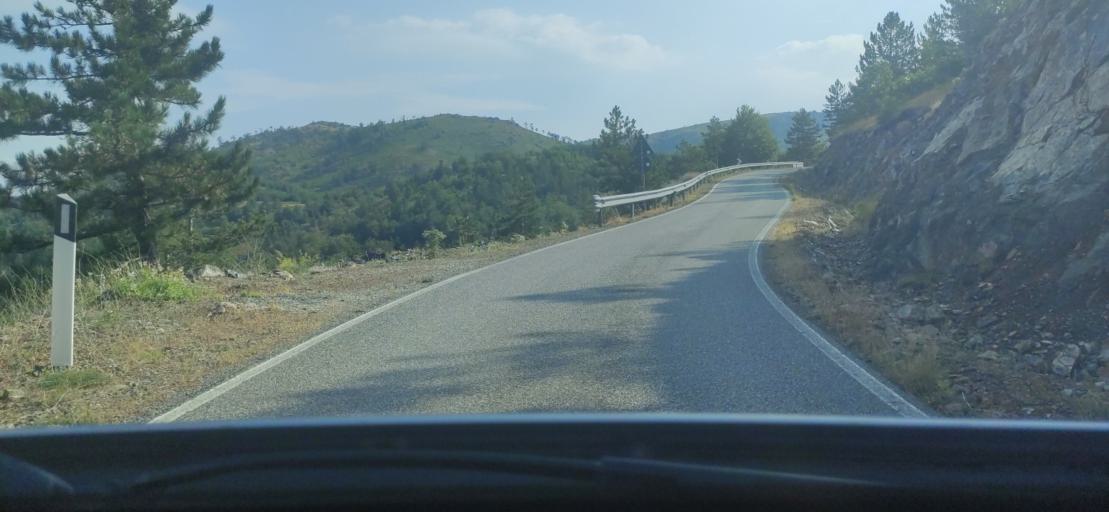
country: AL
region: Shkoder
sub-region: Rrethi i Pukes
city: Iballe
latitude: 42.1708
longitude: 20.0205
